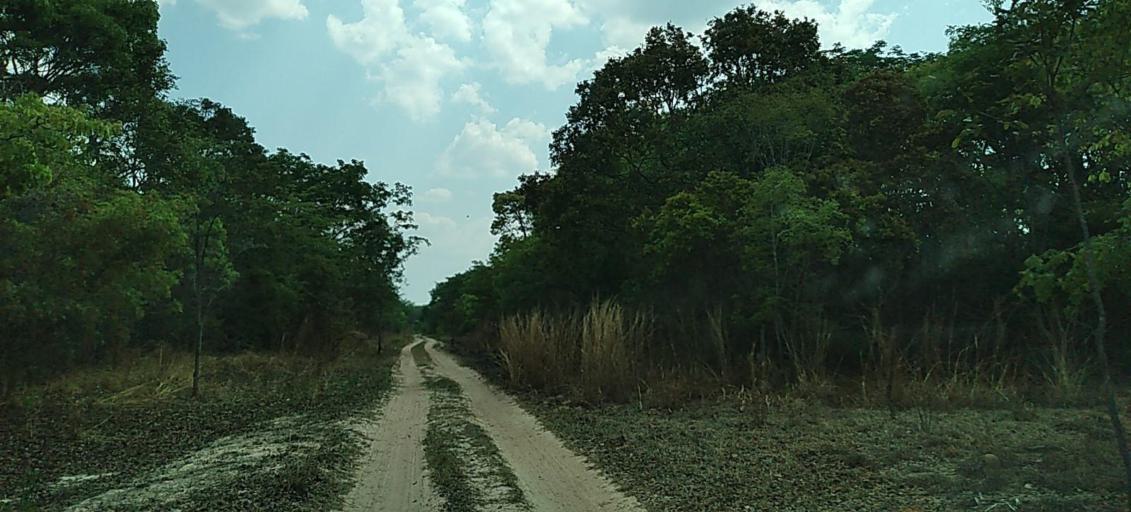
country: ZM
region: Copperbelt
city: Mpongwe
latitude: -13.8577
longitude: 27.9286
